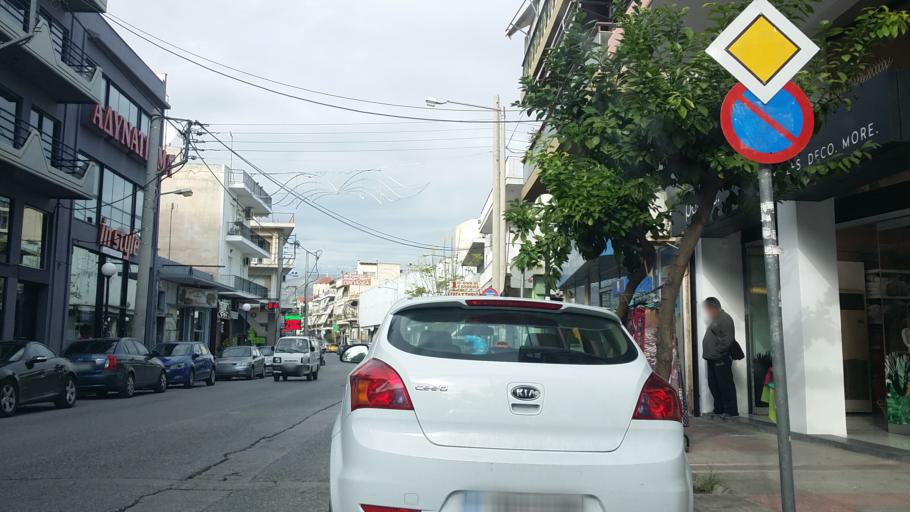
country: GR
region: Attica
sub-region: Nomarchia Athinas
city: Peristeri
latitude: 38.0101
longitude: 23.6936
